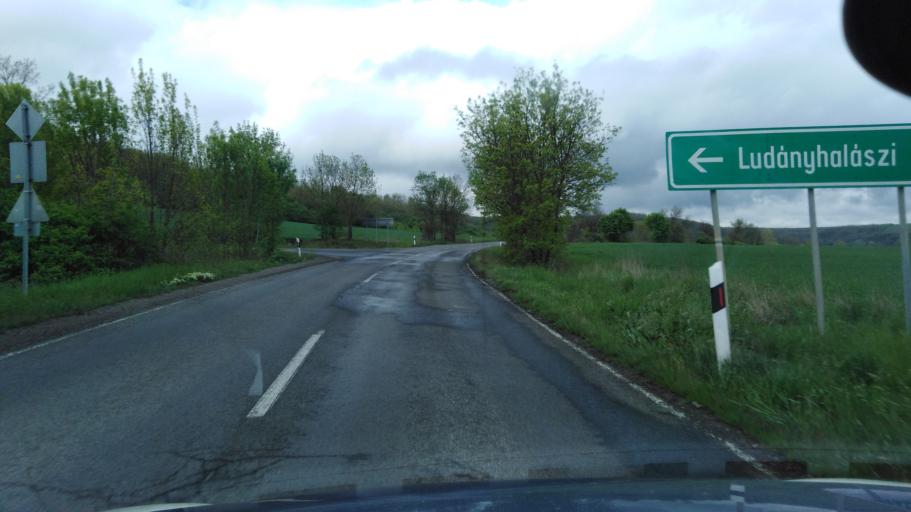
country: HU
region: Nograd
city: Szecseny
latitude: 48.1189
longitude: 19.5490
